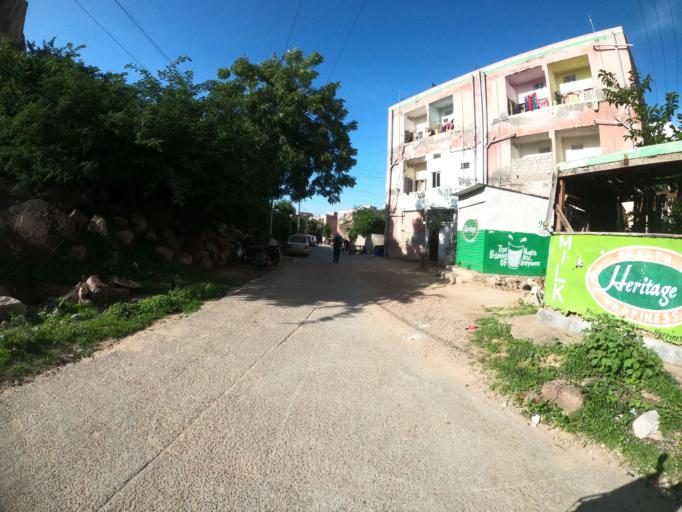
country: IN
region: Telangana
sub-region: Hyderabad
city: Hyderabad
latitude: 17.3591
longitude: 78.3695
